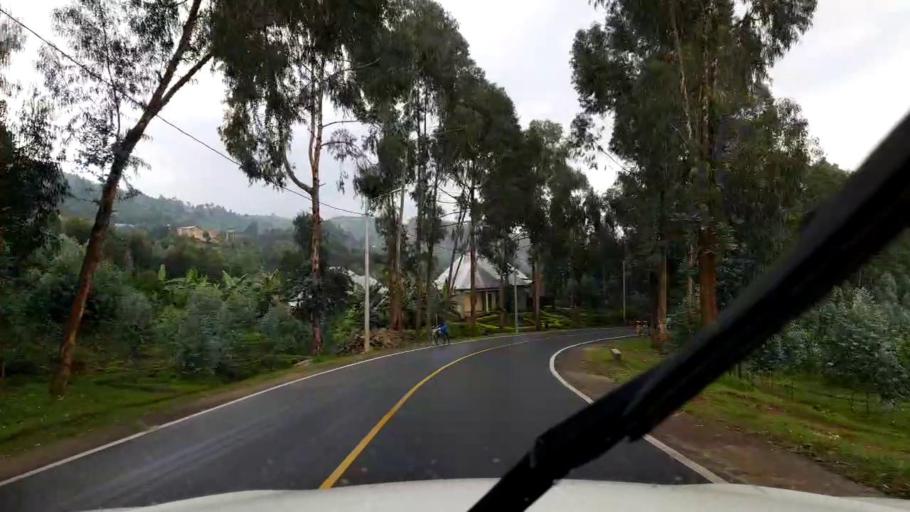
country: RW
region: Western Province
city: Gisenyi
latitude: -1.6744
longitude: 29.3569
